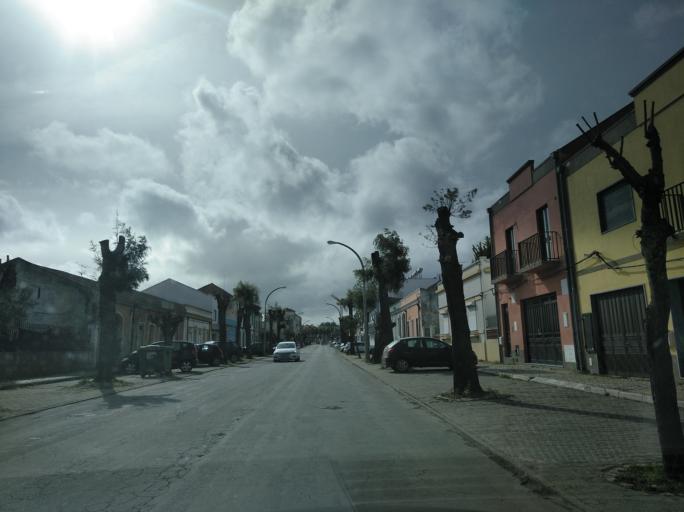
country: PT
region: Setubal
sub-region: Grandola
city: Grandola
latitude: 38.1778
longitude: -8.5639
